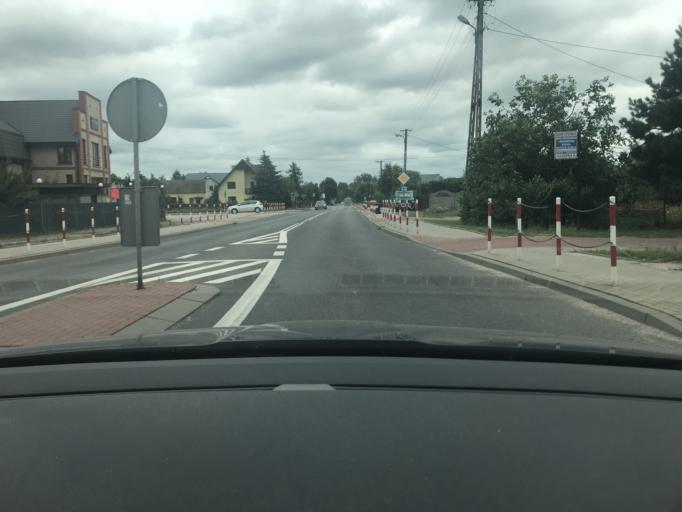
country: PL
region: Lodz Voivodeship
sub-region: Powiat poddebicki
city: Poddebice
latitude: 51.8928
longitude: 18.9628
